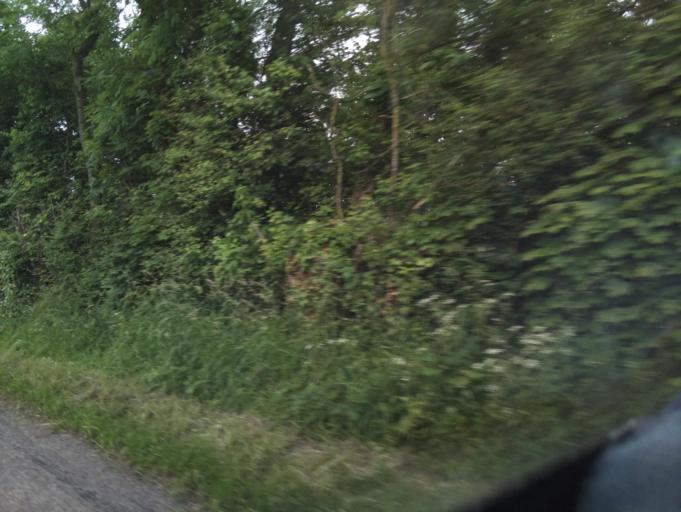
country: GB
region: England
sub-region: District of Rutland
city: Langham
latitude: 52.6817
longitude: -0.8235
